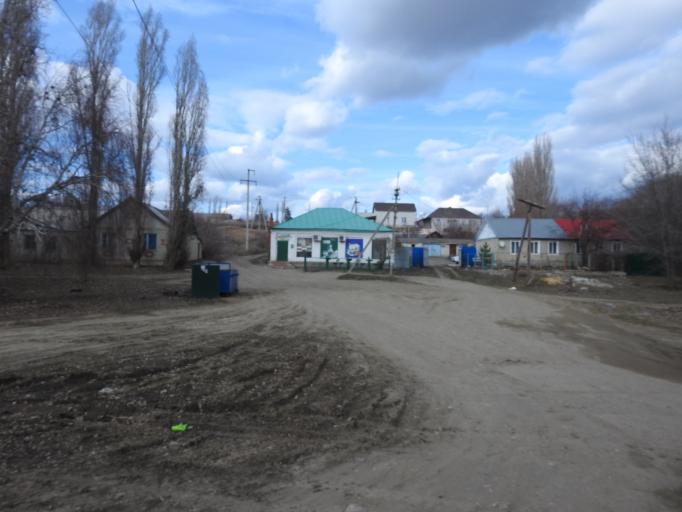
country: RU
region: Saratov
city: Sokolovyy
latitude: 51.3840
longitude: 45.8278
